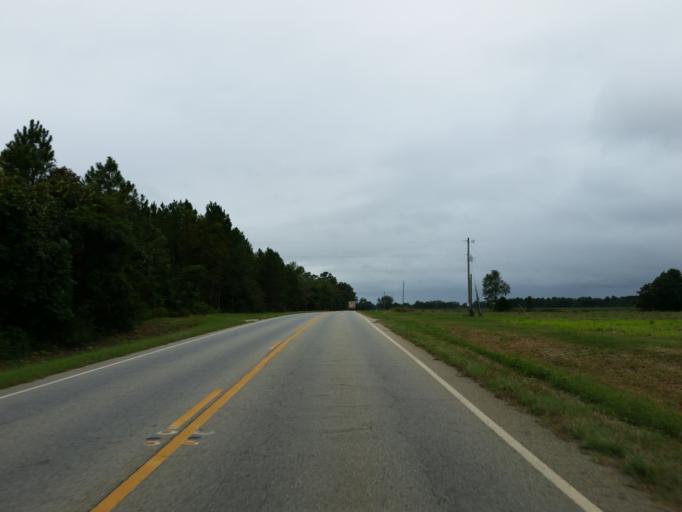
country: US
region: Georgia
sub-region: Cook County
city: Adel
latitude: 31.1323
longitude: -83.3714
